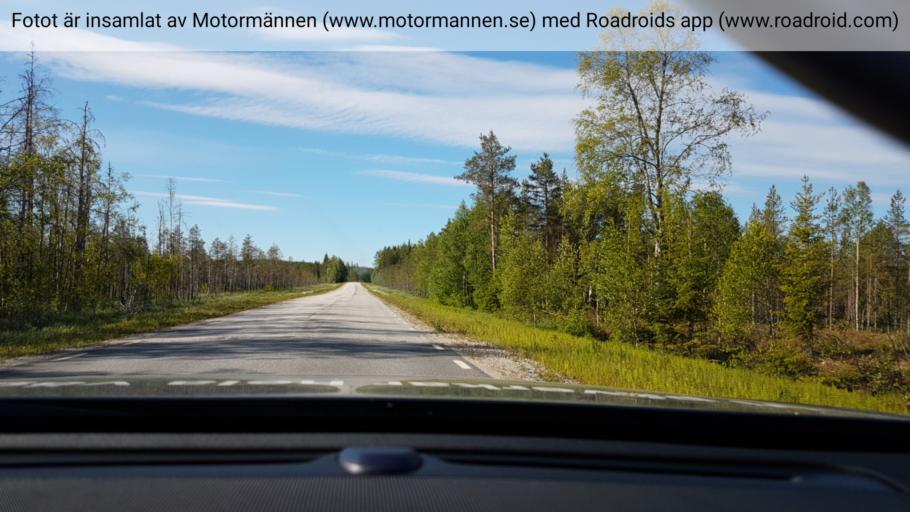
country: SE
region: Vaesterbotten
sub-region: Bjurholms Kommun
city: Bjurholm
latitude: 64.0706
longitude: 19.3406
